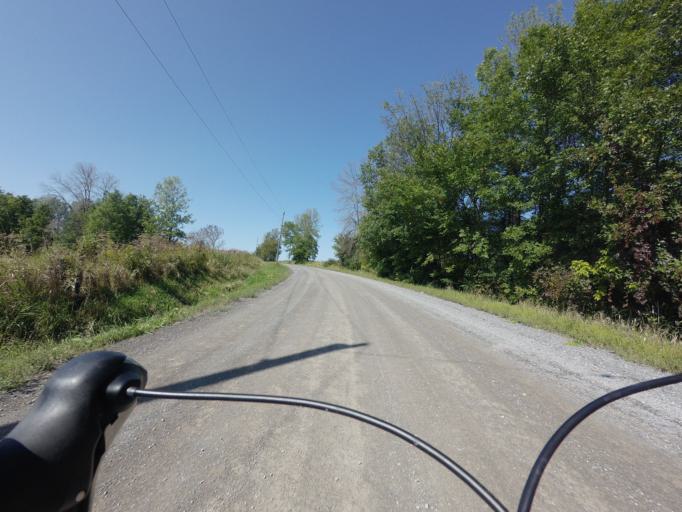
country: CA
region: Ontario
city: Carleton Place
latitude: 45.3552
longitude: -76.0858
